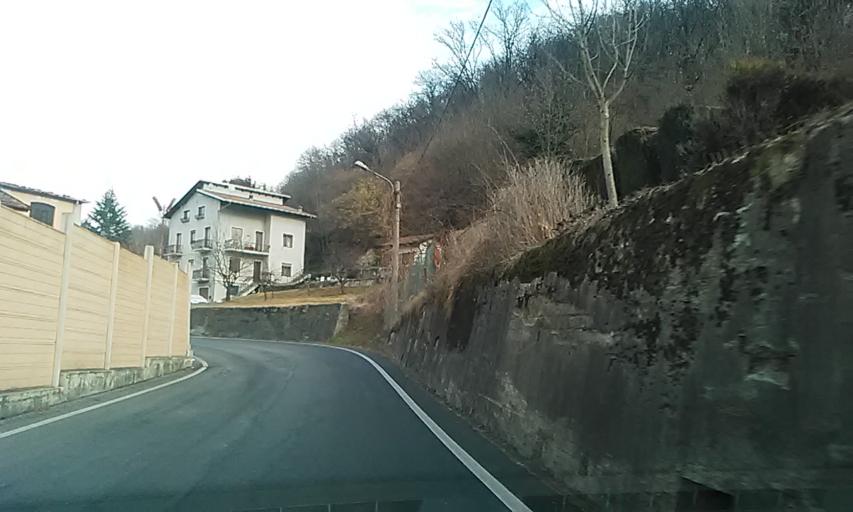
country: IT
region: Piedmont
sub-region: Provincia di Vercelli
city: Borgosesia
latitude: 45.7209
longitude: 8.2832
